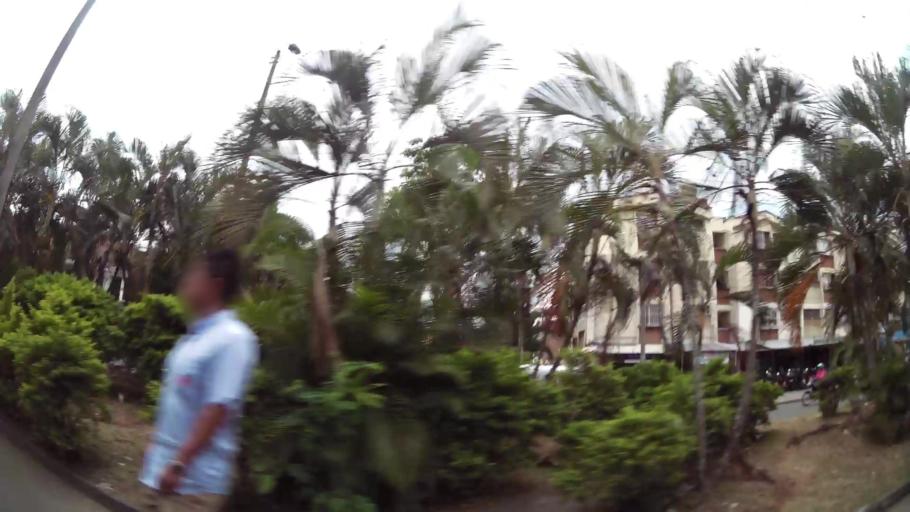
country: CO
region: Valle del Cauca
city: Cali
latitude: 3.4662
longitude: -76.4978
